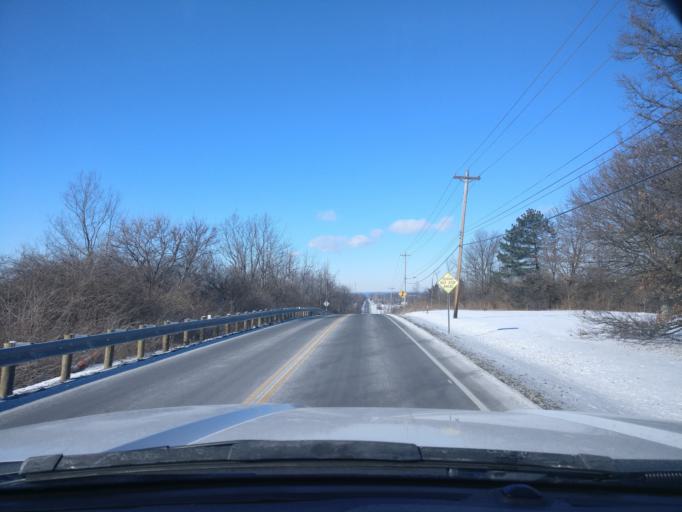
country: US
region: Ohio
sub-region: Warren County
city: Hunter
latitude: 39.5079
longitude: -84.2651
